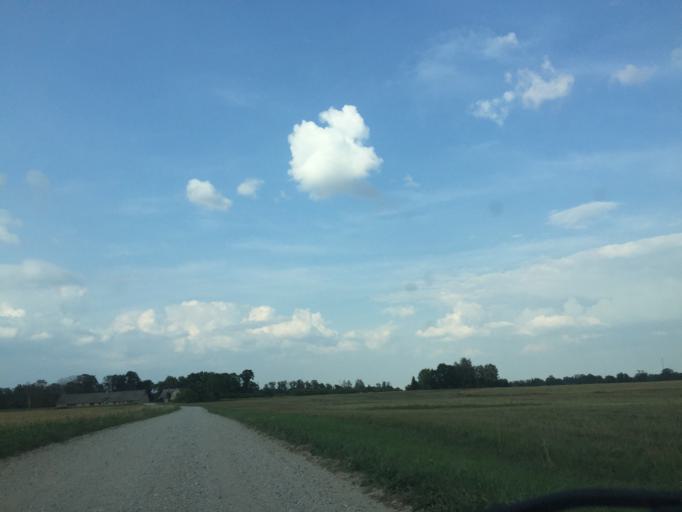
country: LT
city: Zagare
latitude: 56.4803
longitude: 23.1490
